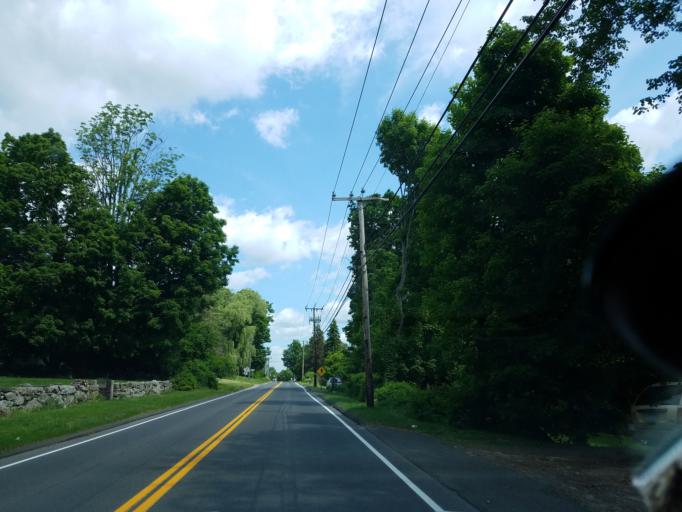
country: US
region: New York
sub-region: Putnam County
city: Putnam Lake
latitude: 41.4523
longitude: -73.5234
